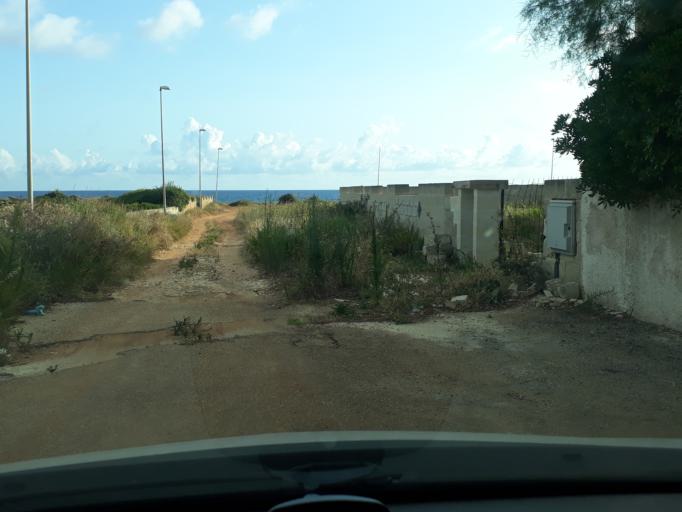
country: IT
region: Apulia
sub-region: Provincia di Brindisi
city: Carovigno
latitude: 40.7631
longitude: 17.6874
